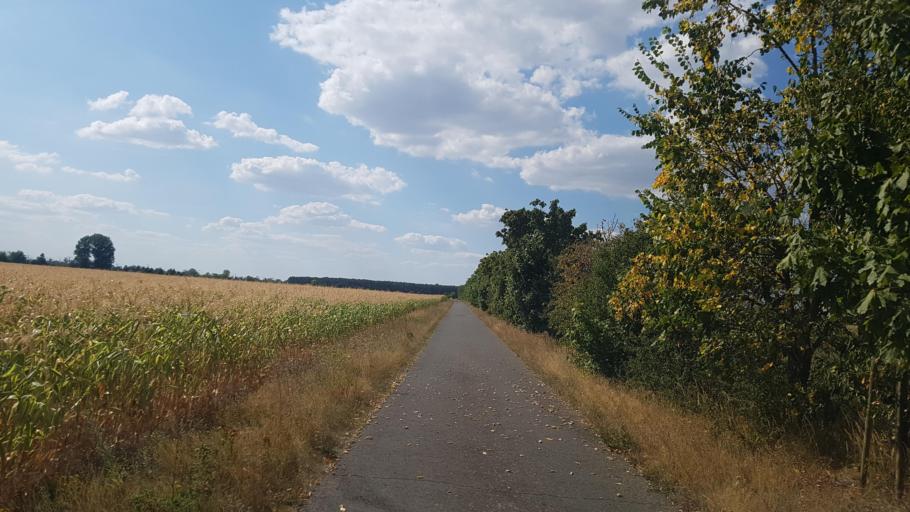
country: DE
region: Saxony-Anhalt
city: Elster
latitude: 51.8381
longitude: 12.8195
